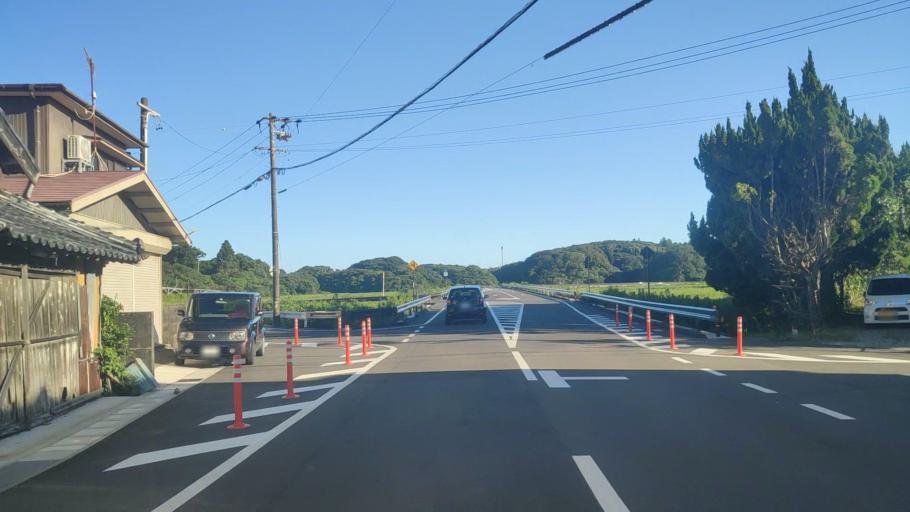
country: JP
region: Mie
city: Toba
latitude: 34.3167
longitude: 136.8850
